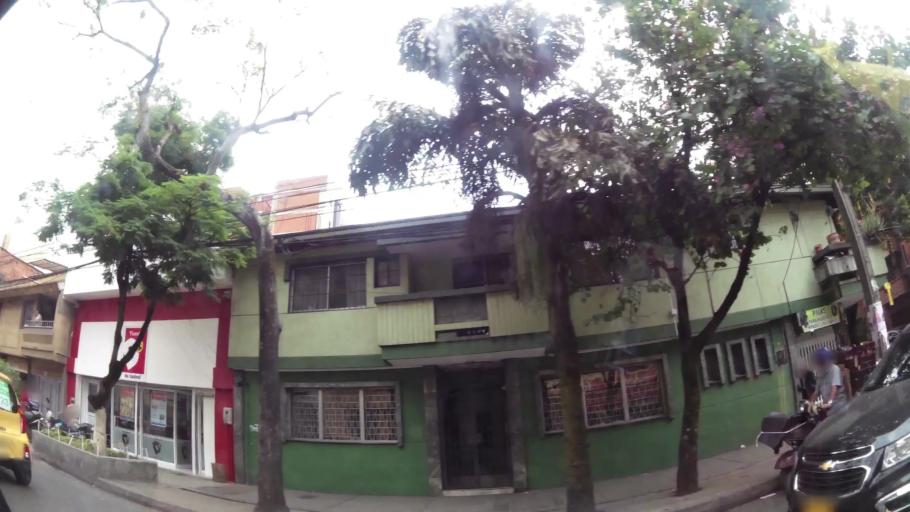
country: CO
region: Antioquia
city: Medellin
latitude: 6.2464
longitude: -75.5591
